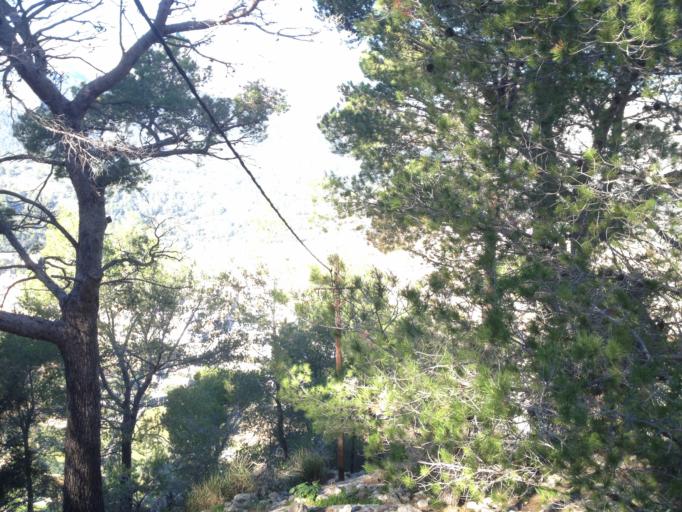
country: ES
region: Balearic Islands
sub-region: Illes Balears
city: Pollenca
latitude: 39.8700
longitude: 3.0218
